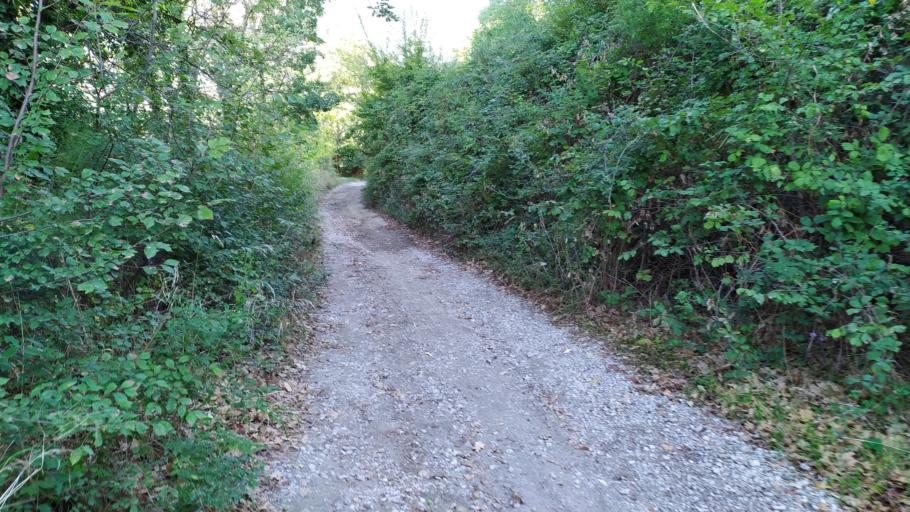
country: IT
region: Campania
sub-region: Provincia di Salerno
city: Siano
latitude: 40.8051
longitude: 14.6684
